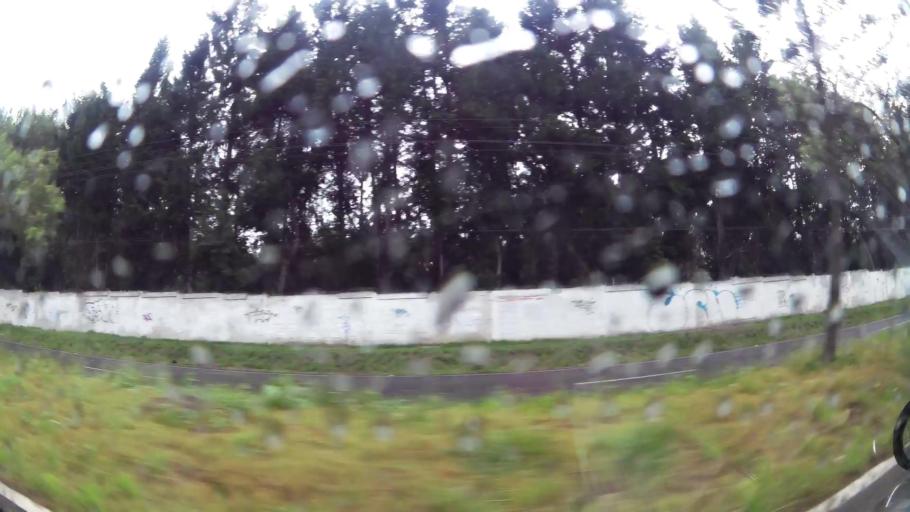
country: EC
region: Pichincha
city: Quito
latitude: -0.0948
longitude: -78.4888
